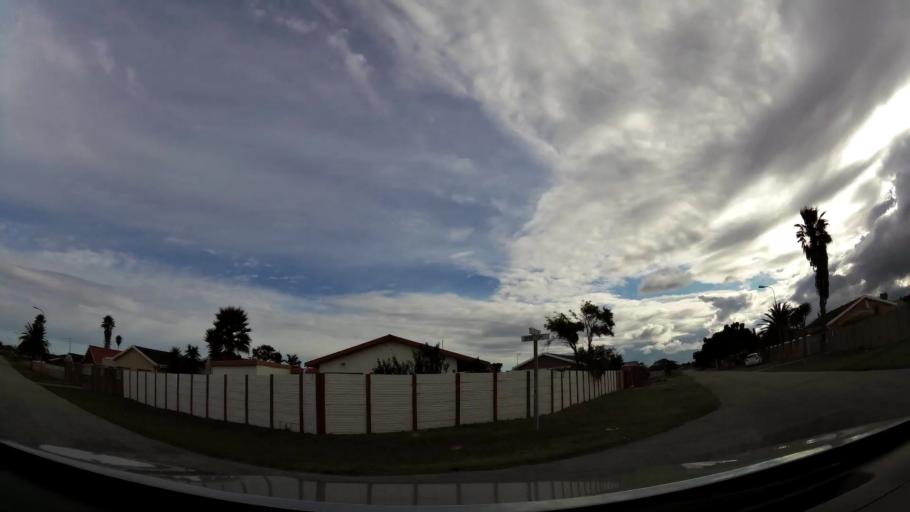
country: ZA
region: Eastern Cape
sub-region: Nelson Mandela Bay Metropolitan Municipality
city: Port Elizabeth
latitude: -33.9362
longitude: 25.4663
